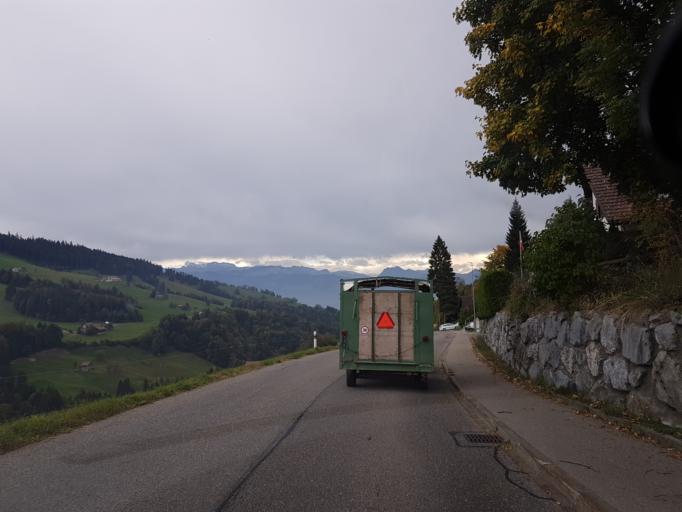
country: CH
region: Saint Gallen
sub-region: Wahlkreis See-Gaster
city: Goldingen
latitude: 47.2823
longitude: 8.9804
